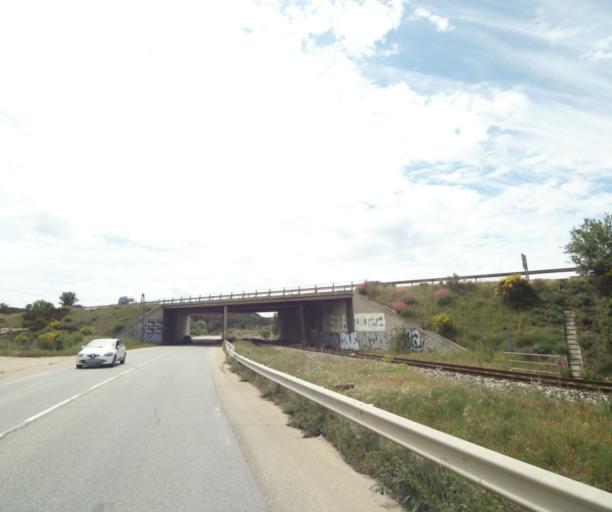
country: FR
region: Provence-Alpes-Cote d'Azur
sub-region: Departement des Bouches-du-Rhone
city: Rognac
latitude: 43.5042
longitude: 5.2381
